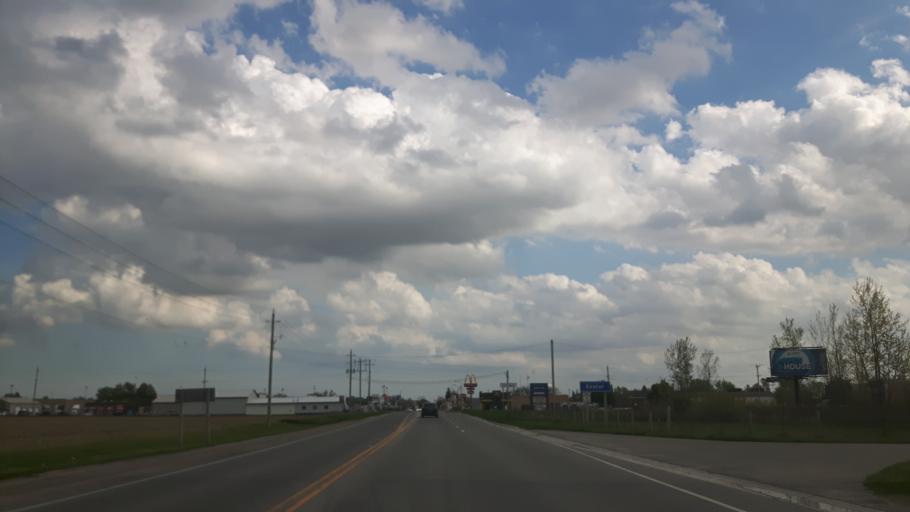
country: CA
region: Ontario
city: South Huron
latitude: 43.3655
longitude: -81.4844
